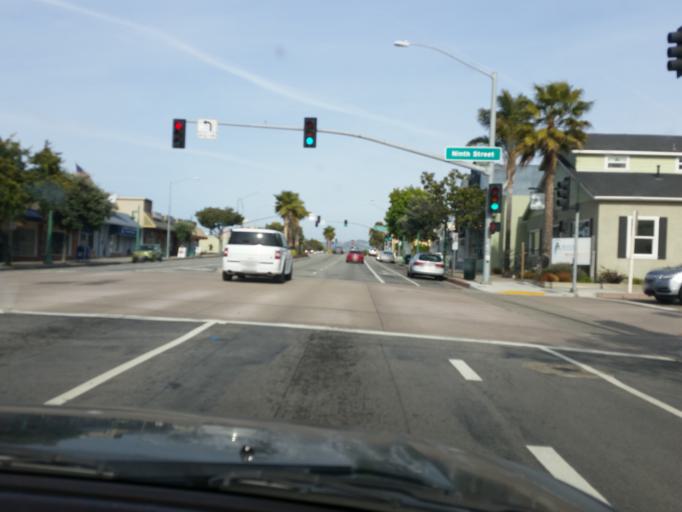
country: US
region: California
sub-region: San Luis Obispo County
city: Grover Beach
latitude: 35.1214
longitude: -120.6205
